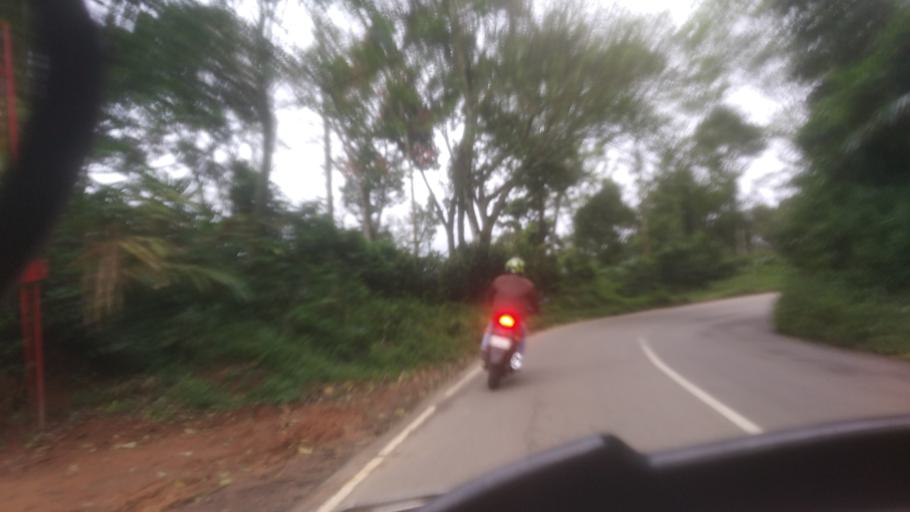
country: IN
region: Tamil Nadu
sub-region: Theni
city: Kombai
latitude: 9.8961
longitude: 77.1740
